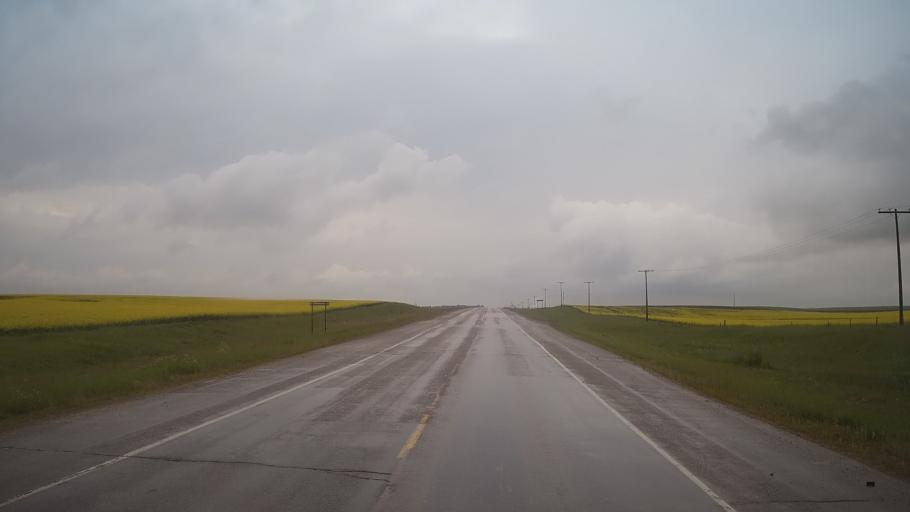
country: CA
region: Saskatchewan
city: Unity
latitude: 52.4350
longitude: -109.0436
